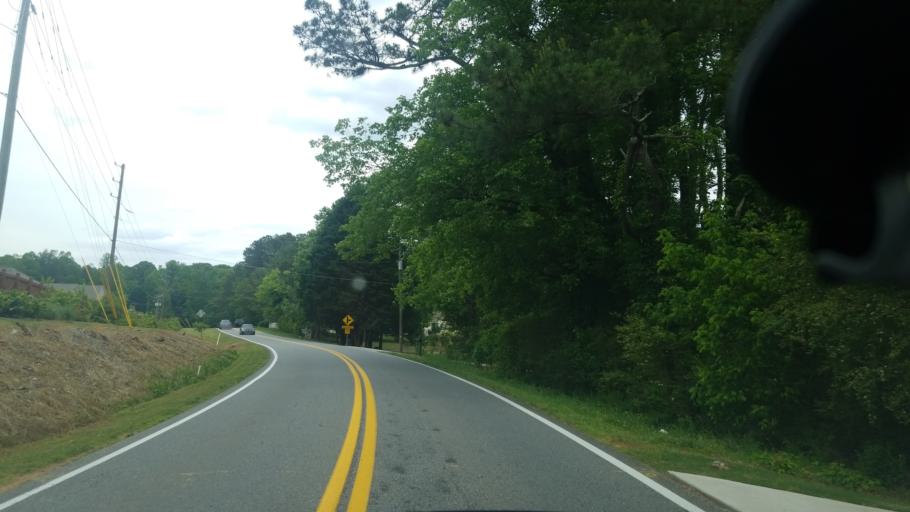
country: US
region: Georgia
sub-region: Forsyth County
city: Cumming
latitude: 34.1507
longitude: -84.1646
